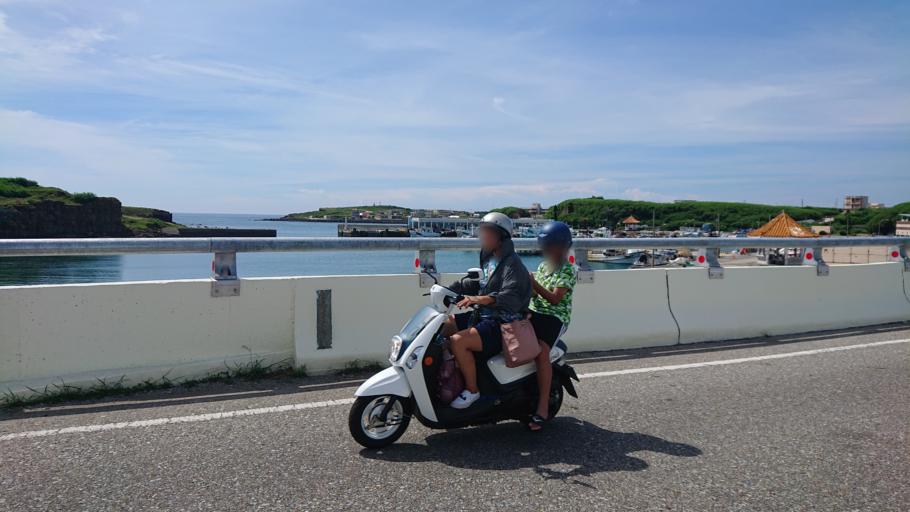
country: TW
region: Taiwan
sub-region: Penghu
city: Ma-kung
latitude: 23.6476
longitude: 119.5194
